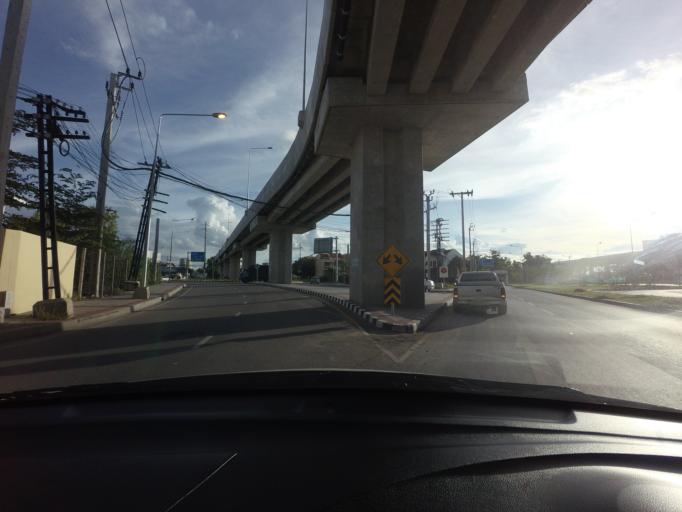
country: TH
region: Nonthaburi
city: Bang Kruai
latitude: 13.7914
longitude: 100.4775
